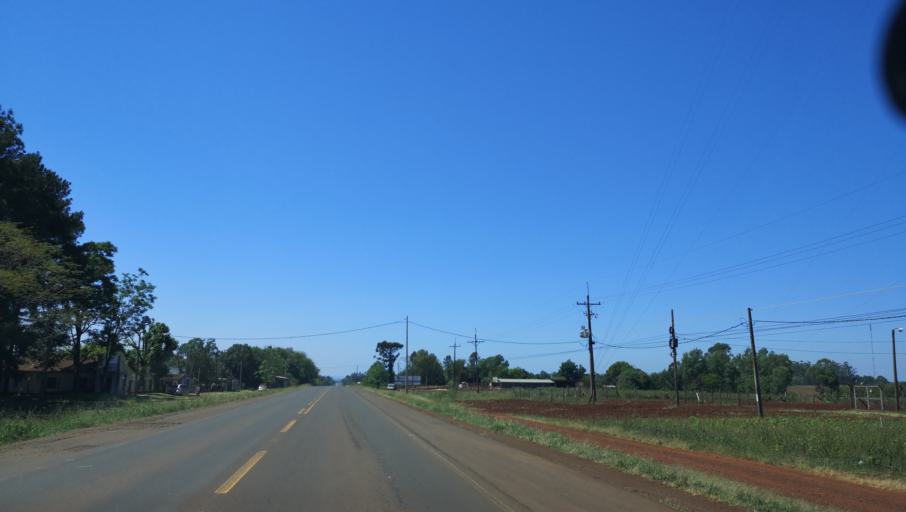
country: PY
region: Itapua
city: San Juan del Parana
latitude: -27.2658
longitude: -55.9602
